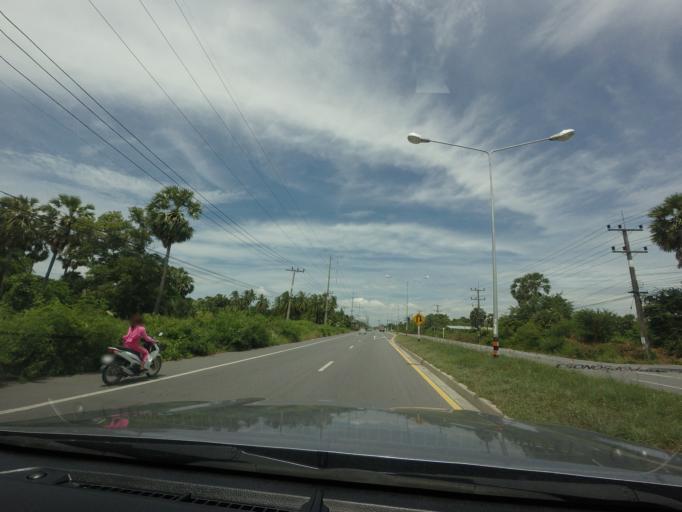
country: TH
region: Songkhla
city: Ranot
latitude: 7.7401
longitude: 100.3646
